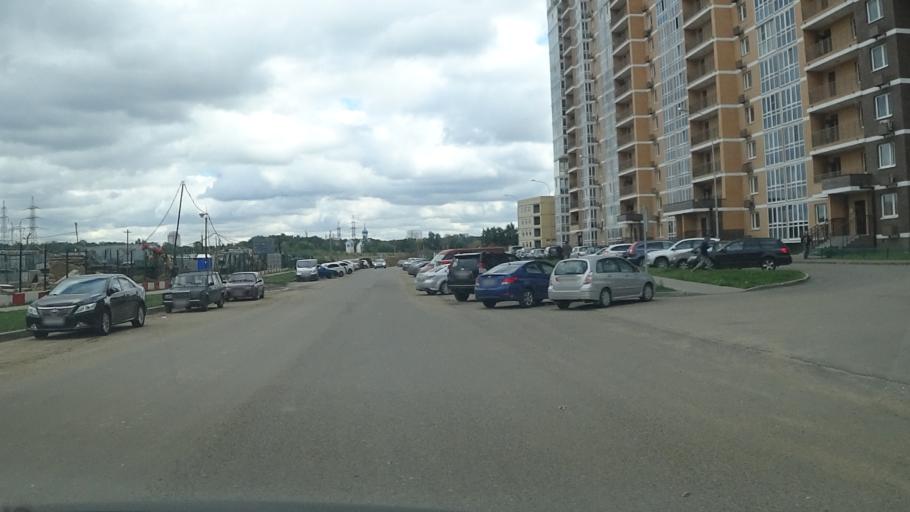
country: RU
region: Moskovskaya
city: Vostryakovo
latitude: 55.6568
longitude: 37.4260
